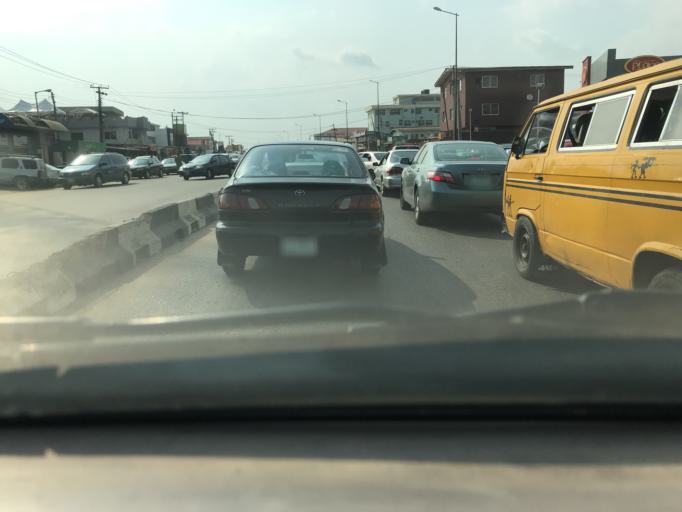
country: NG
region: Lagos
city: Agege
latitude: 6.6024
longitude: 3.3078
